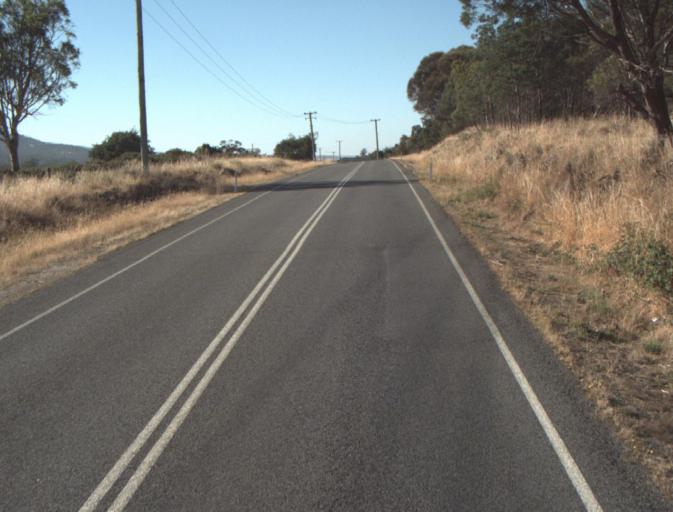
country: AU
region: Tasmania
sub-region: Launceston
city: Newstead
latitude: -41.4349
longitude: 147.2519
